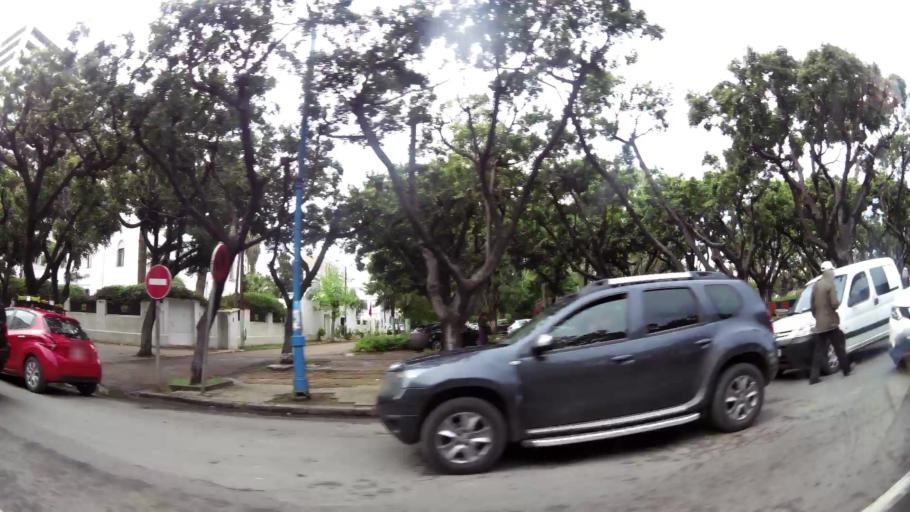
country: MA
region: Grand Casablanca
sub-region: Casablanca
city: Casablanca
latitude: 33.5880
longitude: -7.6217
